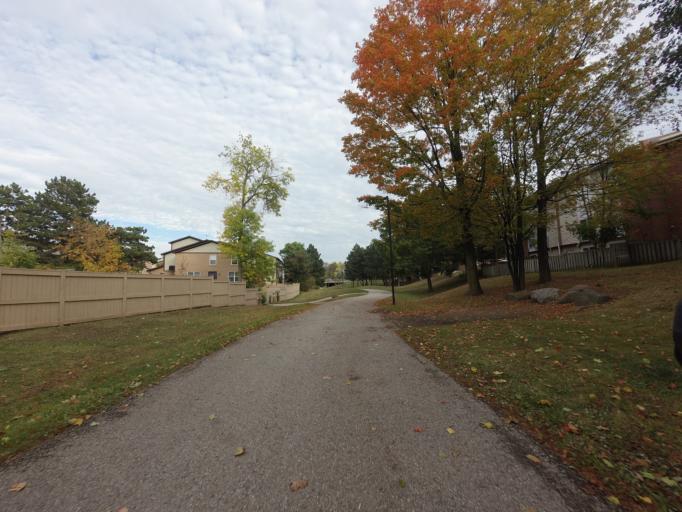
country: CA
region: Ontario
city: Mississauga
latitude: 43.5386
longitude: -79.6842
